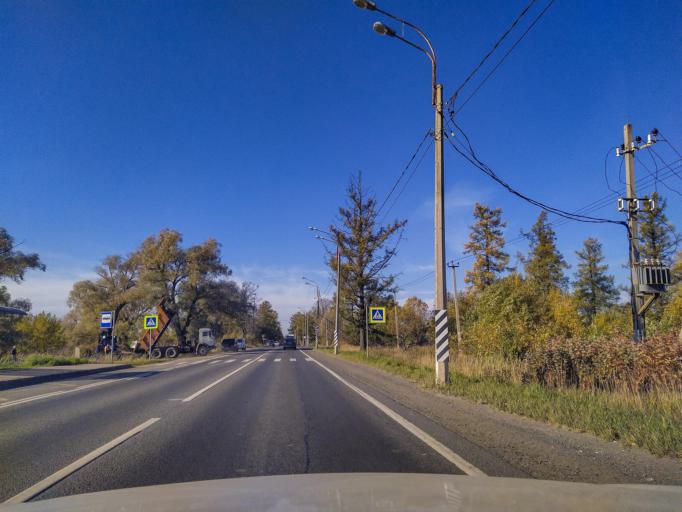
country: RU
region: St.-Petersburg
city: Aleksandrovskaya
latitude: 59.7046
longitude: 30.3451
